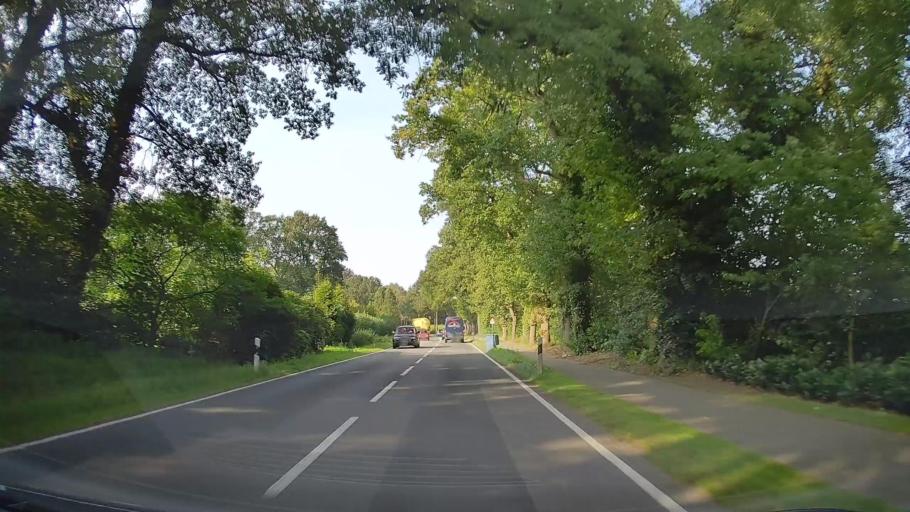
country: DE
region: Lower Saxony
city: Friesoythe
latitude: 53.0910
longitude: 7.8339
